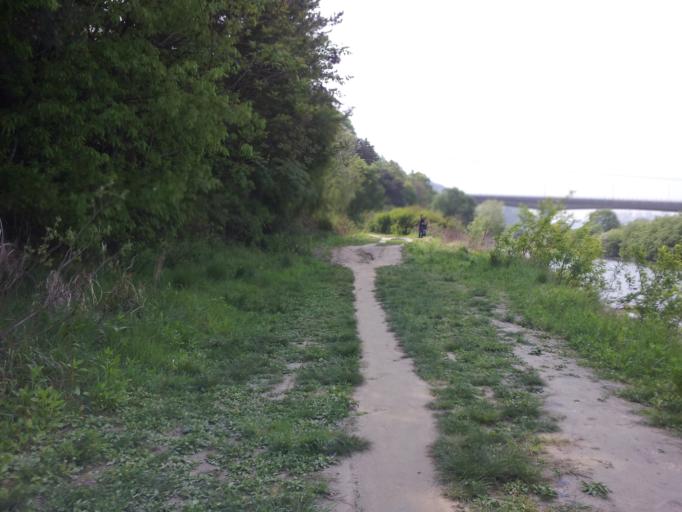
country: KR
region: Daejeon
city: Daejeon
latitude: 36.3351
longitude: 127.3549
